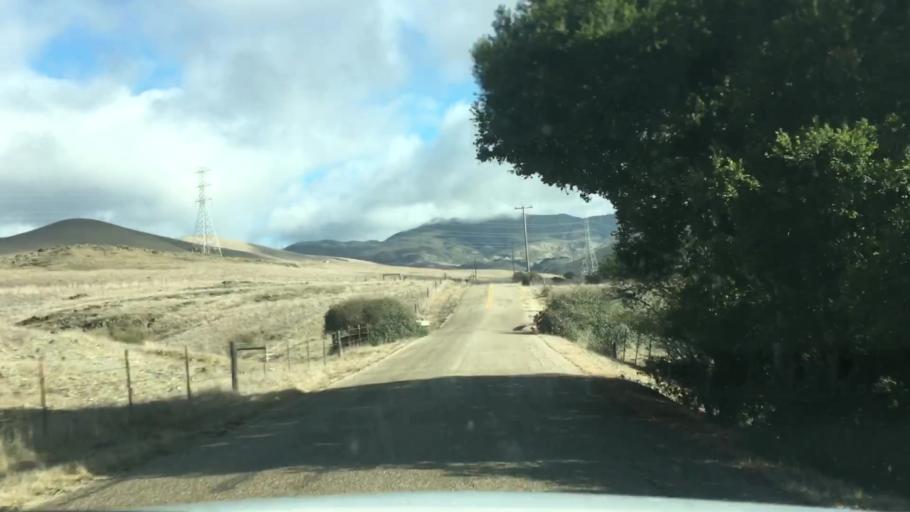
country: US
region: California
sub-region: San Luis Obispo County
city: Morro Bay
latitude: 35.3752
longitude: -120.7949
